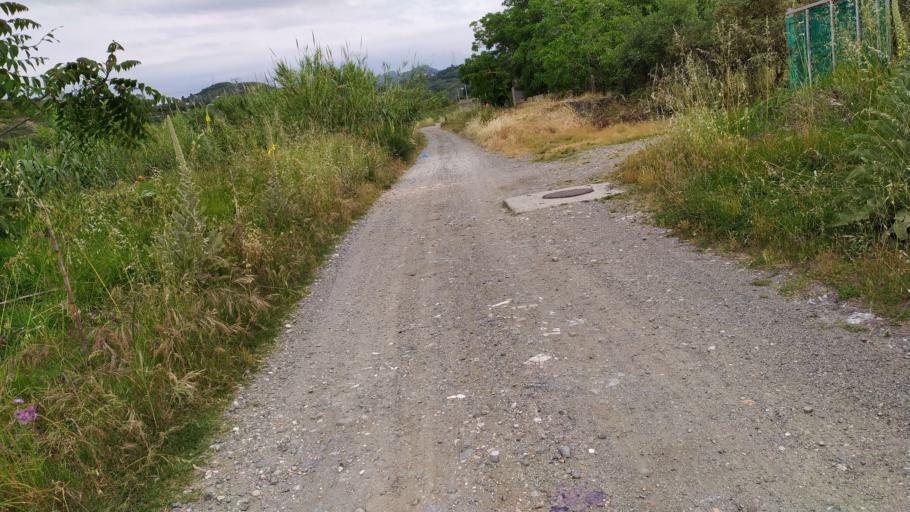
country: IT
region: Sicily
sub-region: Messina
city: San Filippo del Mela
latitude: 38.1761
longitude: 15.2760
